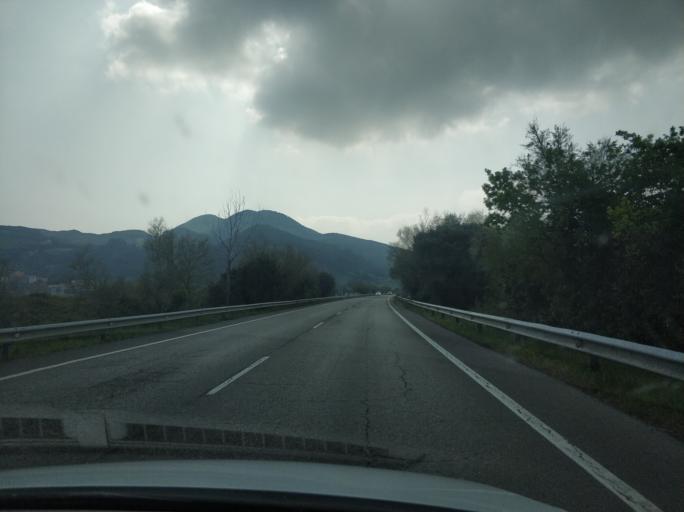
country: ES
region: Cantabria
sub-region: Provincia de Cantabria
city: Santona
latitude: 43.4582
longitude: -3.4654
